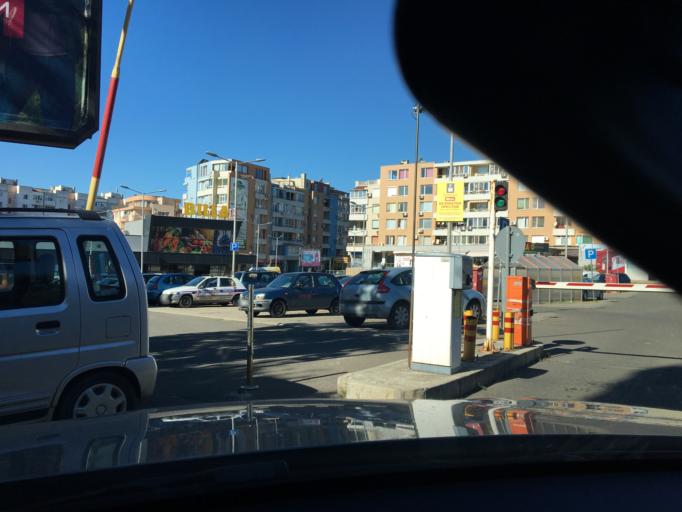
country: BG
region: Burgas
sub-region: Obshtina Burgas
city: Burgas
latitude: 42.5179
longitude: 27.4538
